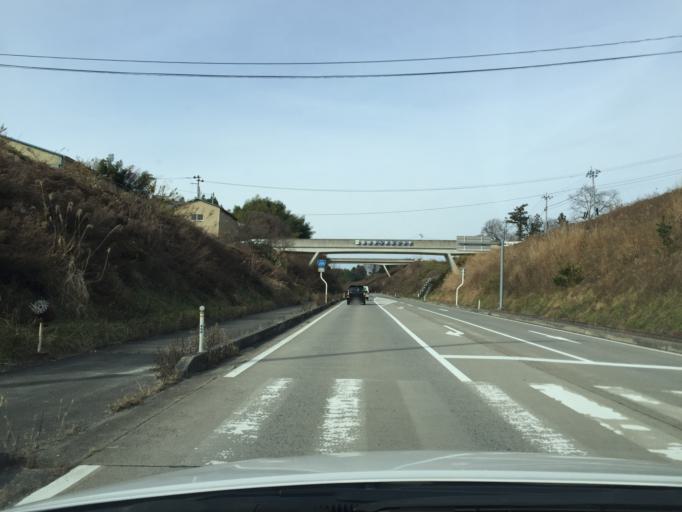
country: JP
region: Fukushima
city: Funehikimachi-funehiki
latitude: 37.4413
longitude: 140.5386
